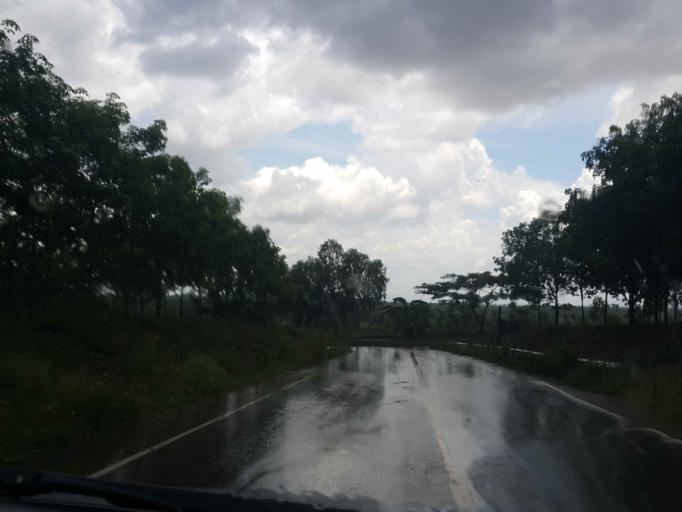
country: TH
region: Phayao
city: Dok Kham Tai
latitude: 19.0346
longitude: 99.9837
